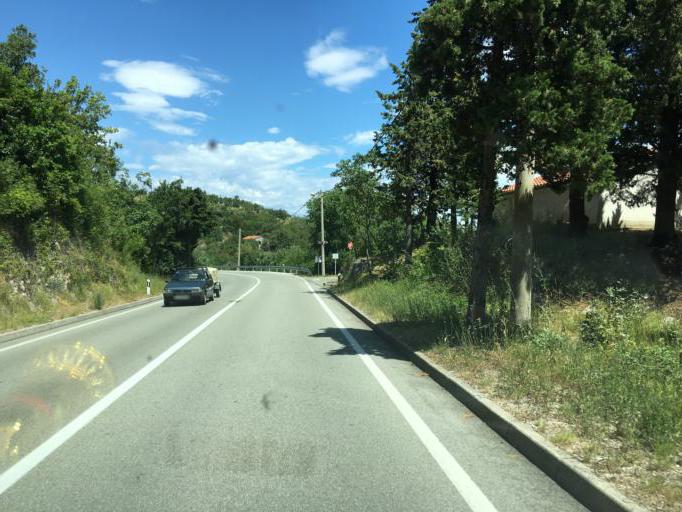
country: HR
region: Istarska
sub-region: Grad Labin
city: Rabac
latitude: 45.1669
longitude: 14.2235
